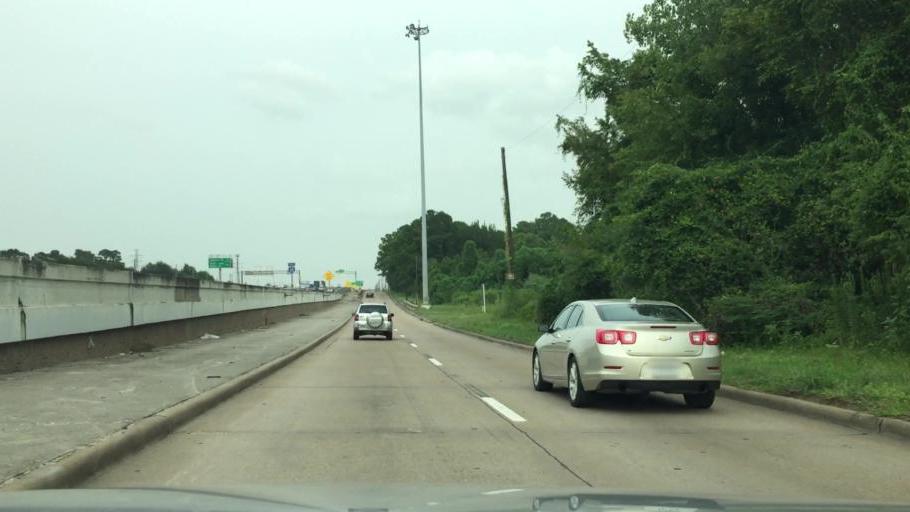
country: US
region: Texas
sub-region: Harris County
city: Cloverleaf
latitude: 29.7728
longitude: -95.1448
